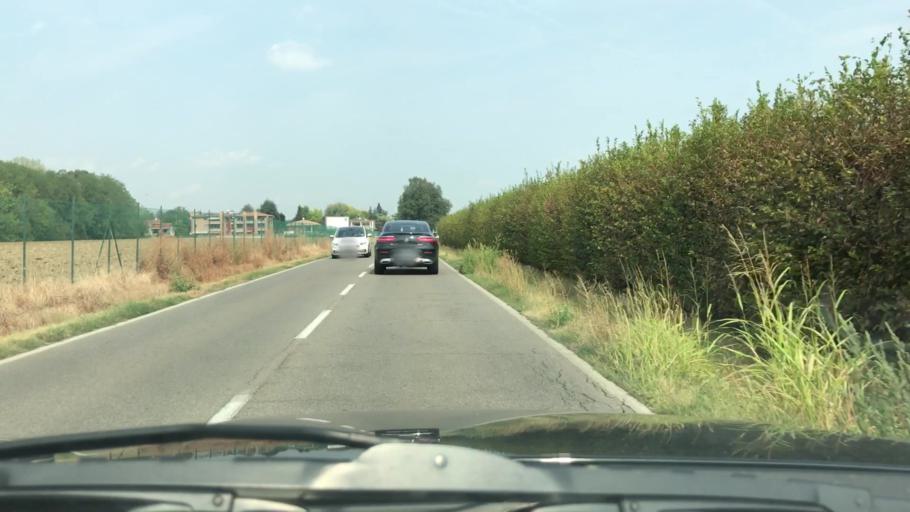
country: IT
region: Emilia-Romagna
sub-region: Provincia di Parma
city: Collecchio
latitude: 44.7386
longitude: 10.2253
